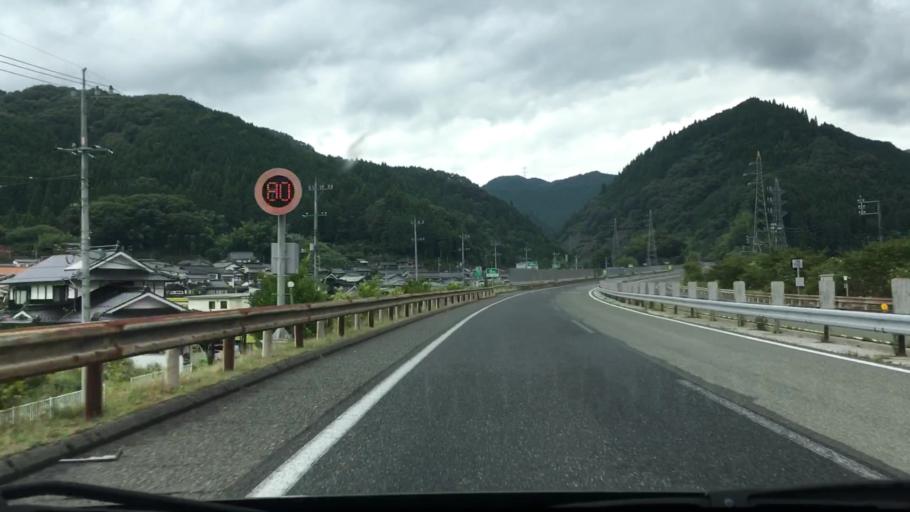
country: JP
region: Okayama
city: Niimi
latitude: 35.0087
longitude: 133.4362
